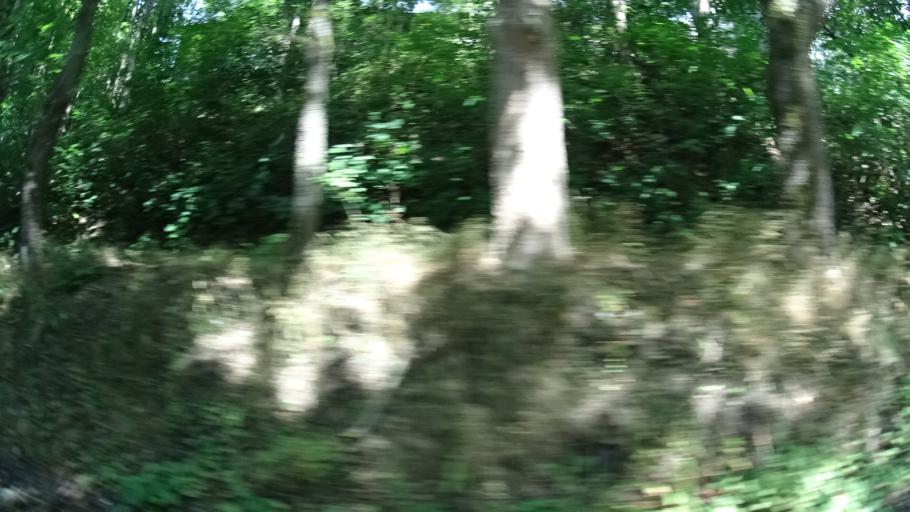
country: DE
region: Thuringia
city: Grossbreitenbach
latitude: 50.5799
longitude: 11.0026
